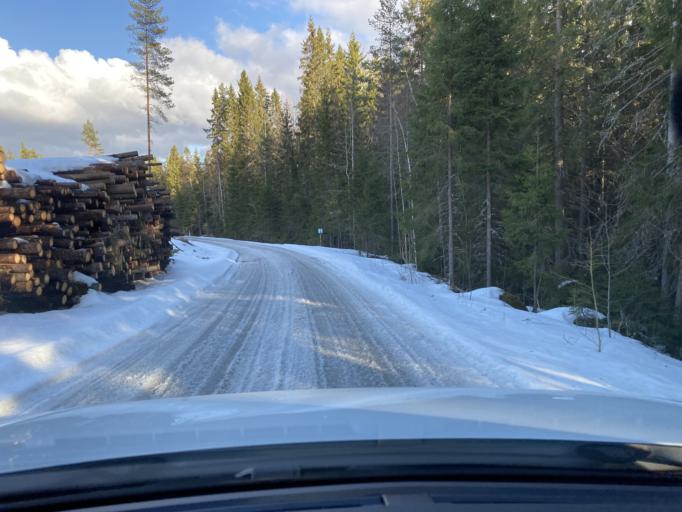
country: FI
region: Pirkanmaa
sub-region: Lounais-Pirkanmaa
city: Mouhijaervi
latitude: 61.4553
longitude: 22.9388
